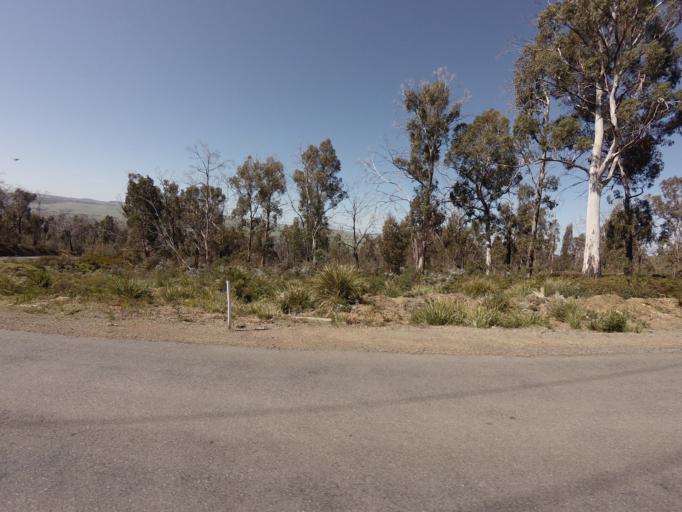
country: AU
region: Tasmania
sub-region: Derwent Valley
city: New Norfolk
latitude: -42.5475
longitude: 146.7134
